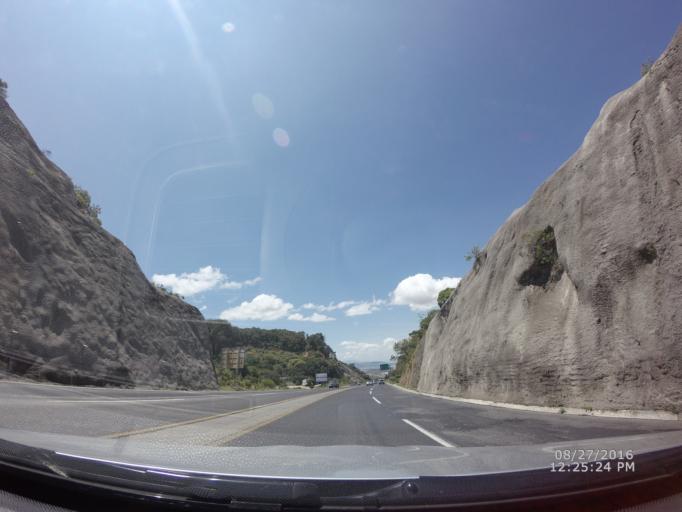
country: MX
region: Hidalgo
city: Mineral del Monte
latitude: 20.1361
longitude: -98.6907
